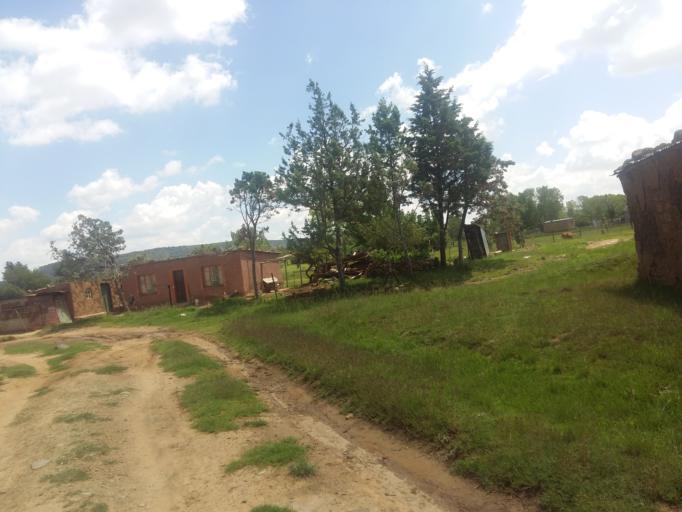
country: LS
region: Mafeteng
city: Mafeteng
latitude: -29.7602
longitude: 27.1127
